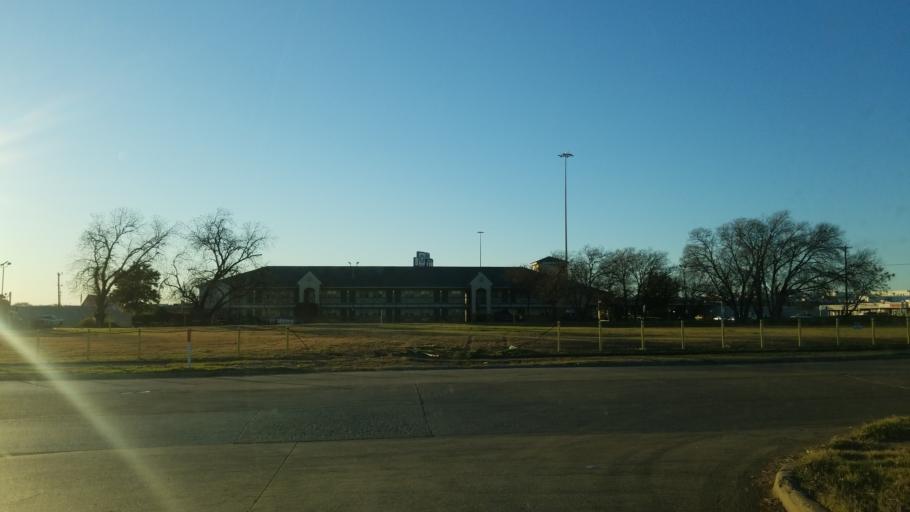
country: US
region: Texas
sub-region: Tarrant County
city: Arlington
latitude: 32.7353
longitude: -97.0595
